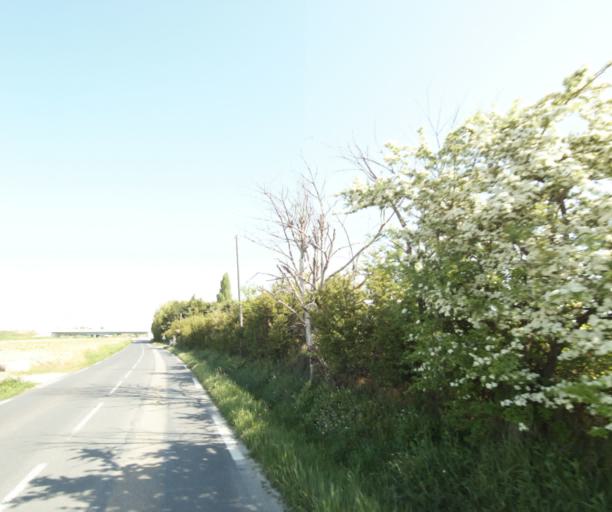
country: FR
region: Languedoc-Roussillon
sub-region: Departement de l'Herault
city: Lattes
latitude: 43.5842
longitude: 3.9088
